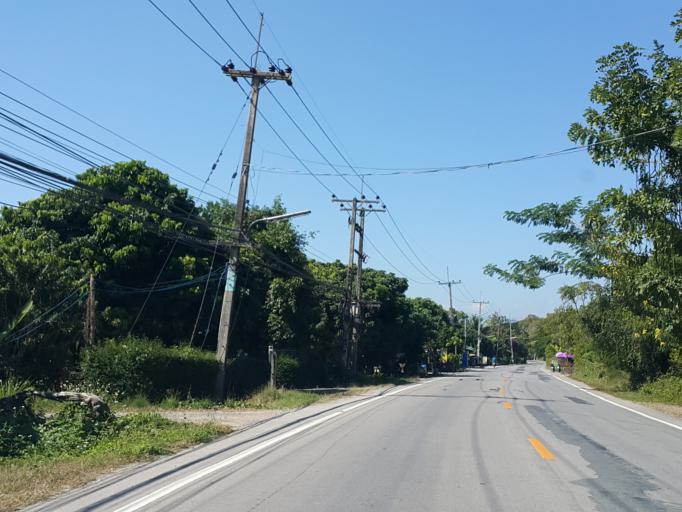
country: TH
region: Chiang Mai
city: San Kamphaeng
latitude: 18.7236
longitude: 99.1692
